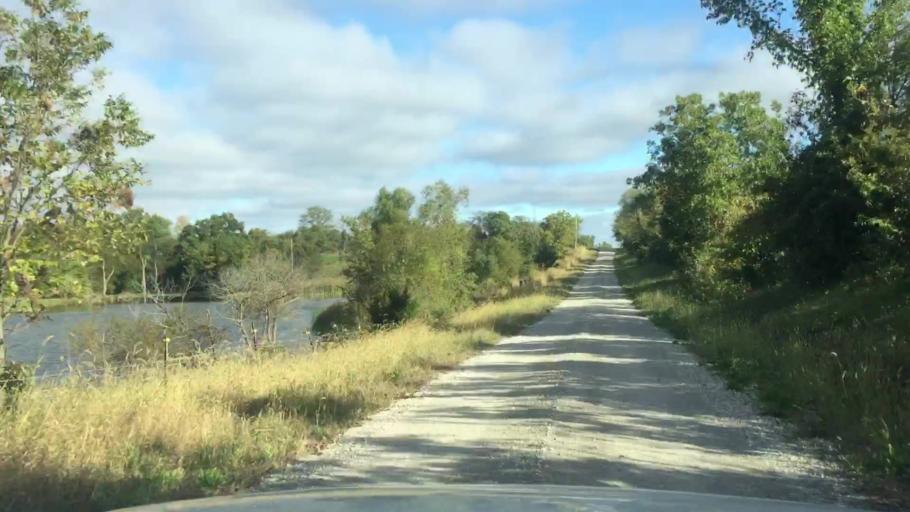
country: US
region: Missouri
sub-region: Howard County
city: New Franklin
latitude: 39.0915
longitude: -92.7797
